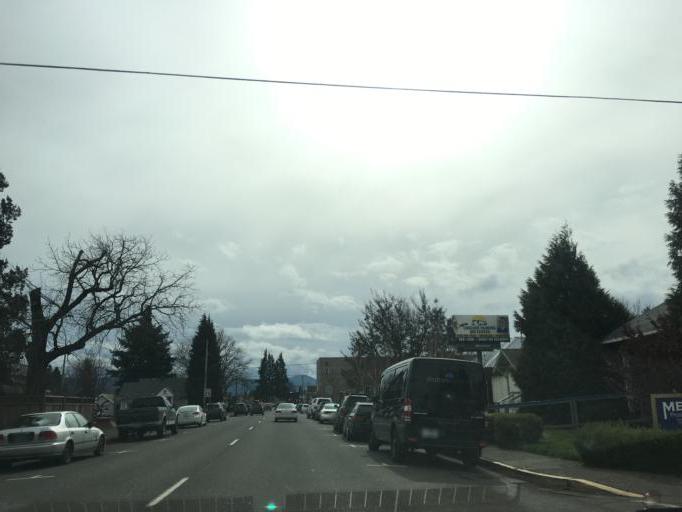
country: US
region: Oregon
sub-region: Hood River County
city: Hood River
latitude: 45.7017
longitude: -121.5247
